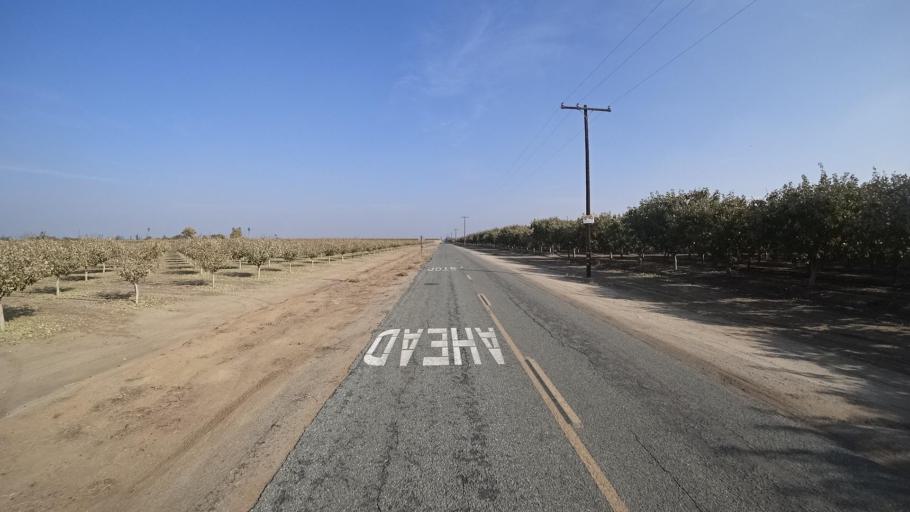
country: US
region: California
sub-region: Tulare County
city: Richgrove
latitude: 35.7908
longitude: -119.1133
